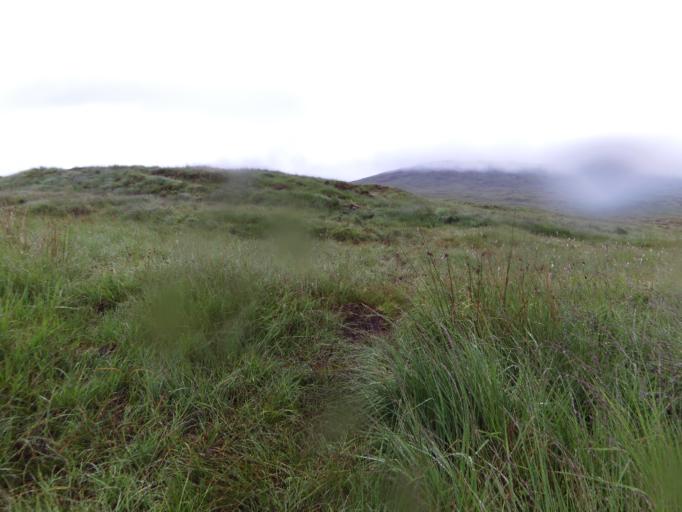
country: GB
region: Scotland
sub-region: Highland
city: Spean Bridge
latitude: 56.7746
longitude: -4.7147
